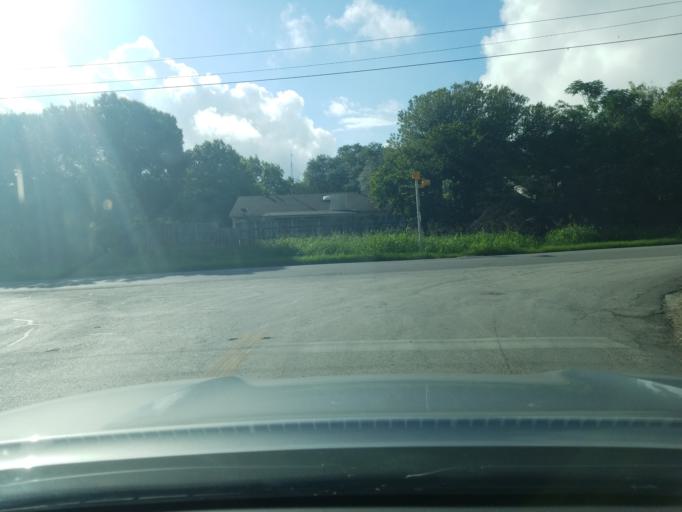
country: US
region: Texas
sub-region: Bexar County
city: Live Oak
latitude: 29.5956
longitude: -98.3613
